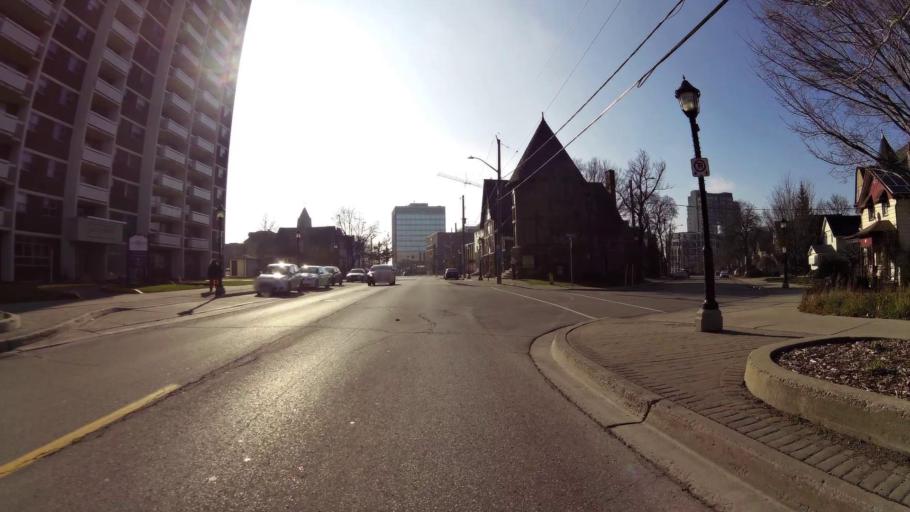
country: CA
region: Ontario
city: Waterloo
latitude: 43.4538
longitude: -80.4934
